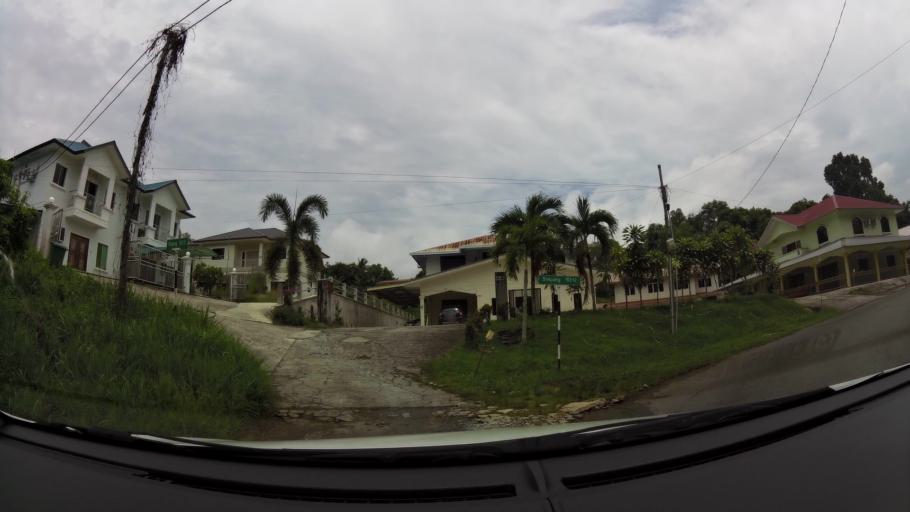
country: BN
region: Brunei and Muara
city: Bandar Seri Begawan
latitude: 4.8918
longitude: 114.9248
